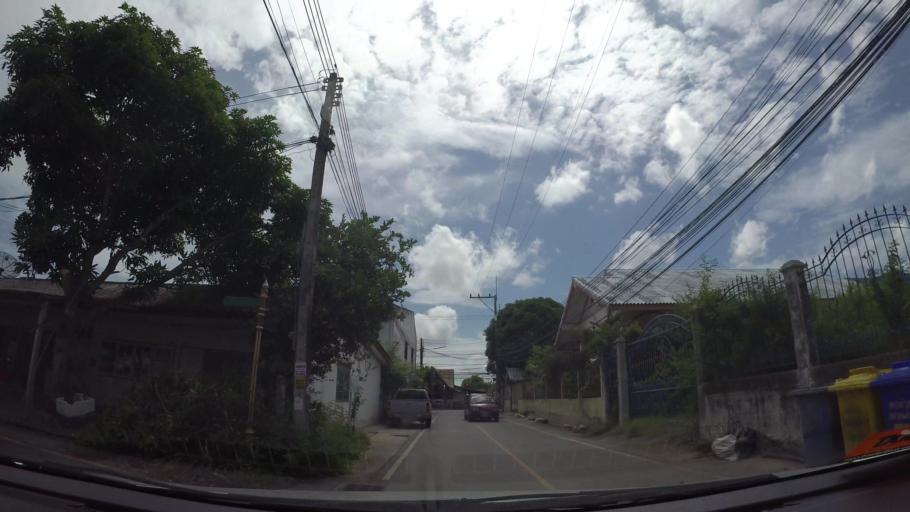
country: TH
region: Chon Buri
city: Sattahip
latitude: 12.6837
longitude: 100.9050
